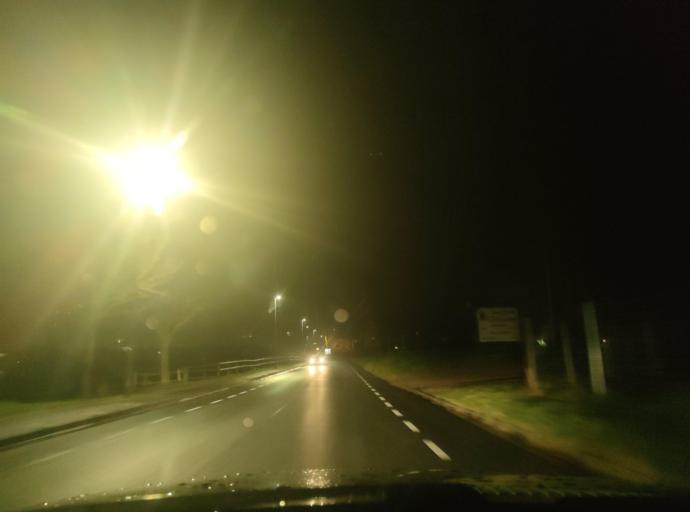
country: DE
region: North Rhine-Westphalia
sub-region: Regierungsbezirk Munster
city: Gelsenkirchen
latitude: 51.4600
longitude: 7.1029
